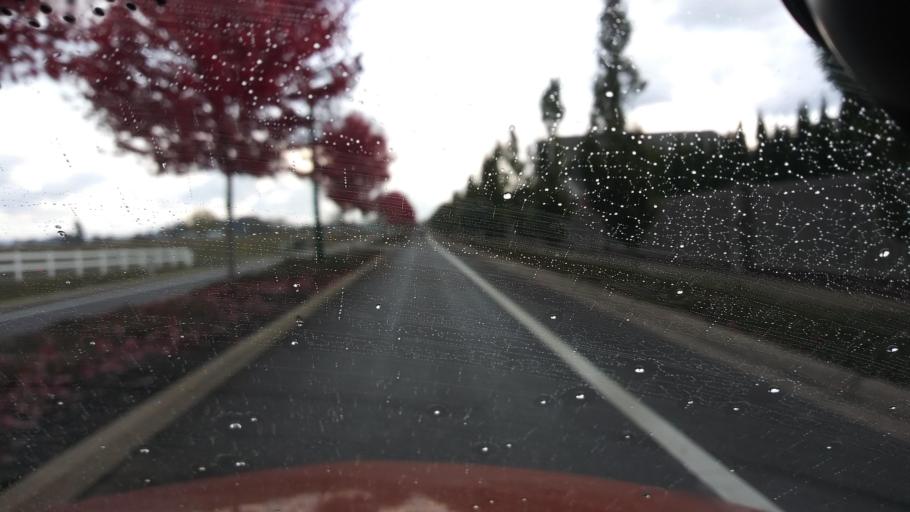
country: US
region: Oregon
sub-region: Washington County
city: Forest Grove
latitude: 45.5391
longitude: -123.1158
